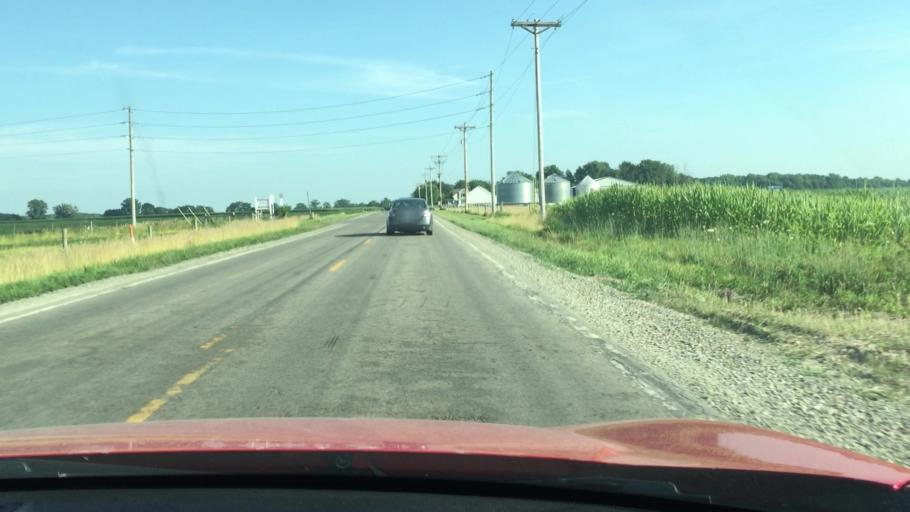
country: US
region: Ohio
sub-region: Hardin County
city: Ada
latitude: 40.6606
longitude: -83.8514
